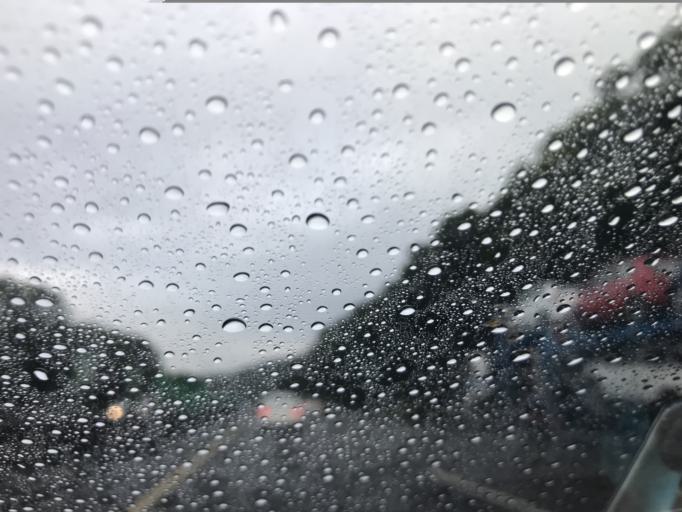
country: TW
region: Taiwan
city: Daxi
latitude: 24.8031
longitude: 121.1689
